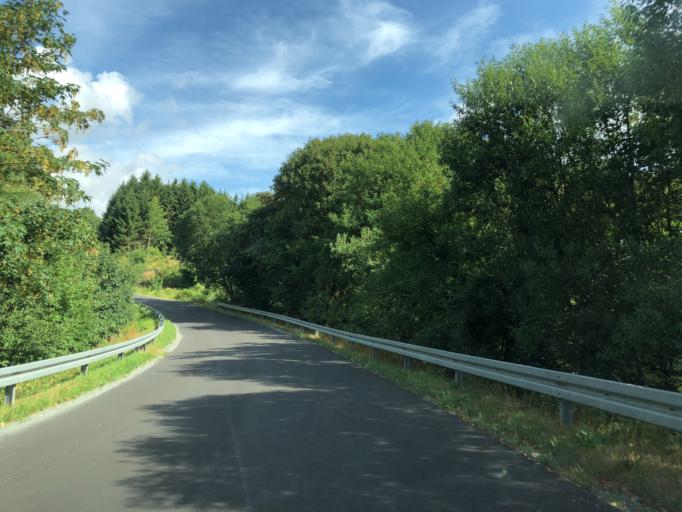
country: DK
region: South Denmark
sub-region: Vejle Kommune
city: Egtved
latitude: 55.6366
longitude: 9.3087
